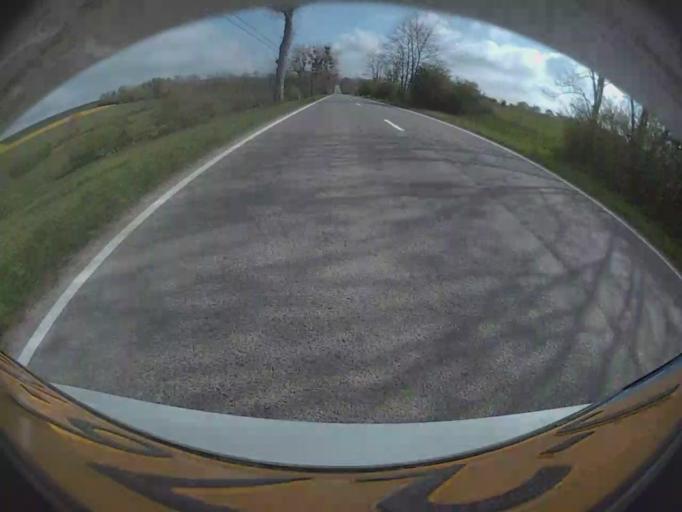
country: BE
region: Wallonia
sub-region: Province de Namur
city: Somme-Leuze
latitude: 50.3281
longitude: 5.3569
